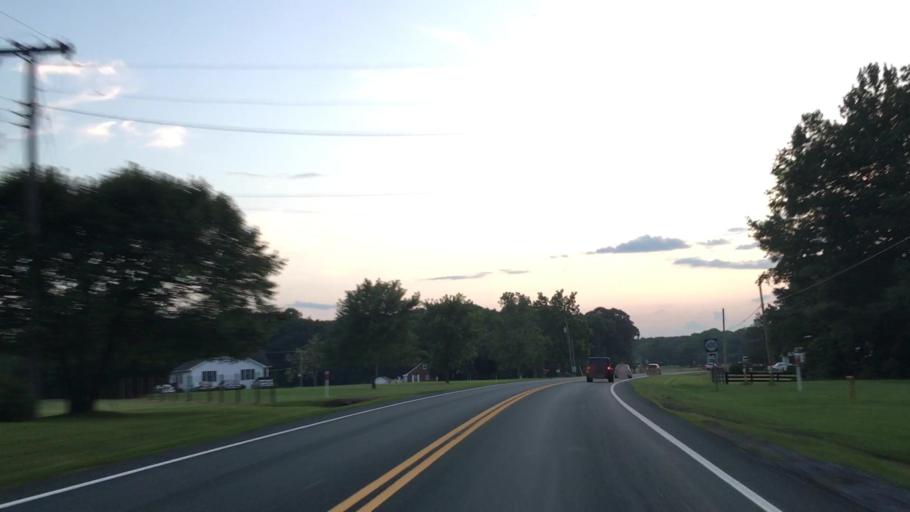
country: US
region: Virginia
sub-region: Orange County
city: Orange
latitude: 38.2555
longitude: -78.0206
